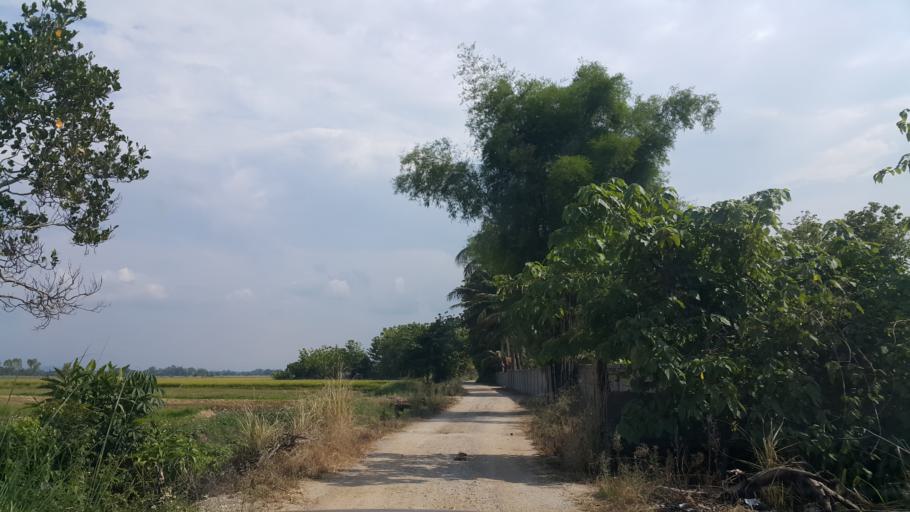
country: TH
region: Chiang Rai
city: Wiang Chai
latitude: 19.9229
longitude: 99.9192
